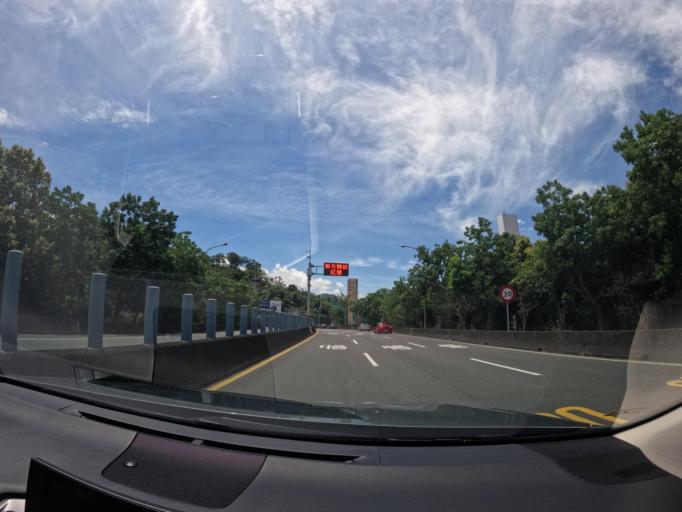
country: TW
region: Taiwan
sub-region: Miaoli
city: Miaoli
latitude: 24.4568
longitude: 120.8774
